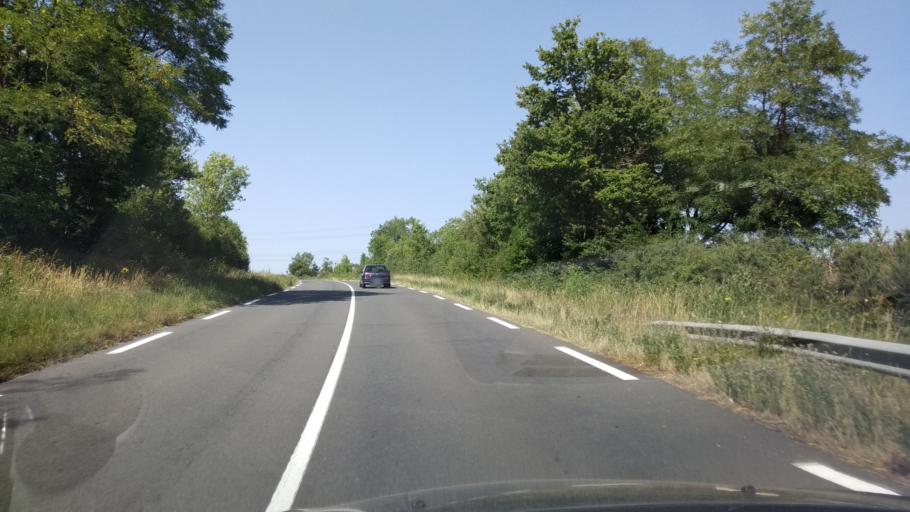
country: FR
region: Poitou-Charentes
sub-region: Departement de la Vienne
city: Lussac-les-Chateaux
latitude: 46.4247
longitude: 0.6370
